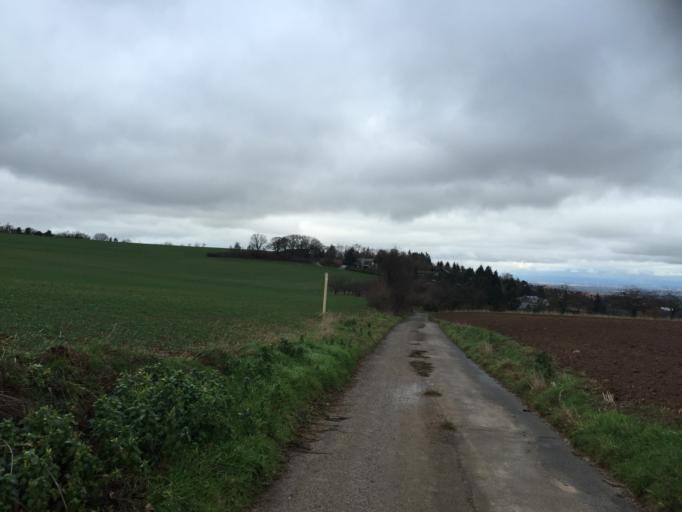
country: DE
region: Rheinland-Pfalz
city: Neuleiningen
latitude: 49.5269
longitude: 8.1269
